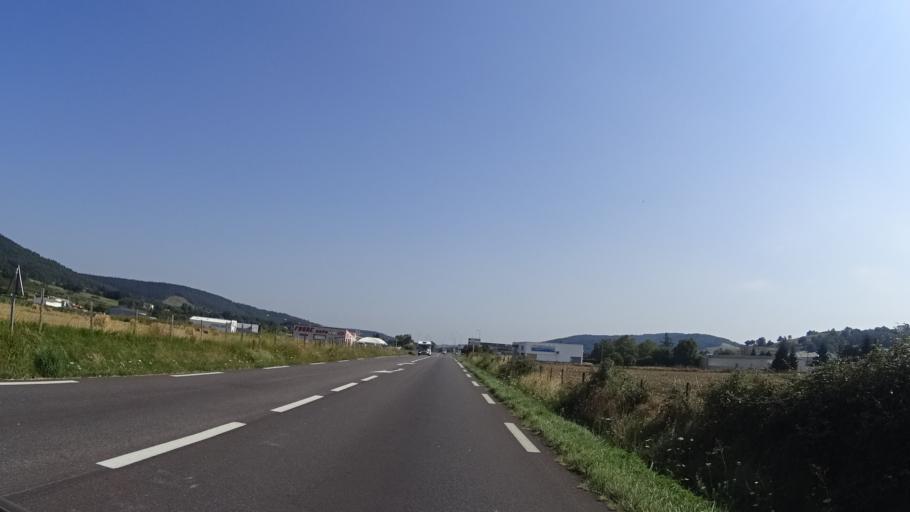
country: FR
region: Midi-Pyrenees
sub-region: Departement de l'Ariege
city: Lavelanet
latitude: 42.9827
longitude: 1.8706
